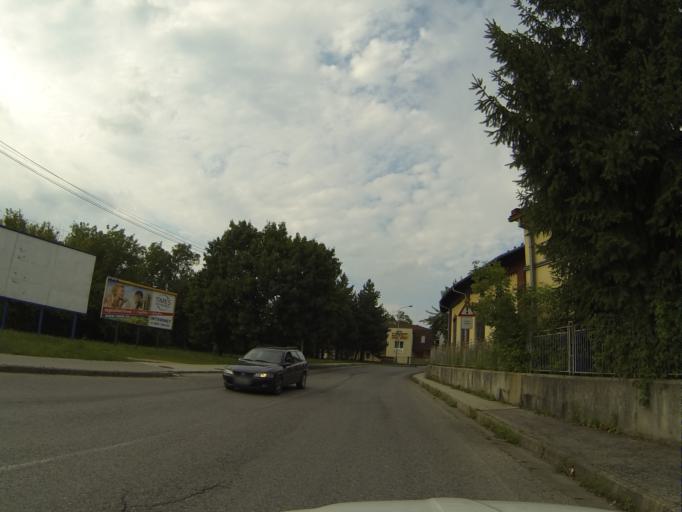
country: SK
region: Nitriansky
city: Prievidza
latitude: 48.7740
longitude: 18.6144
